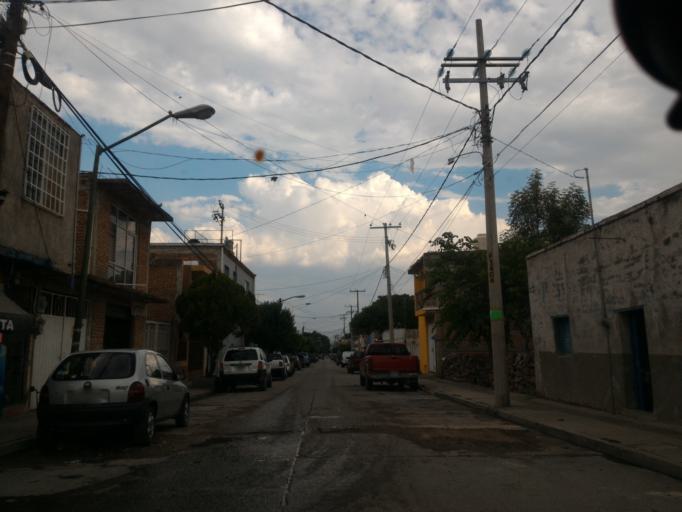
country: MX
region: Guanajuato
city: San Francisco del Rincon
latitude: 21.0328
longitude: -101.8577
